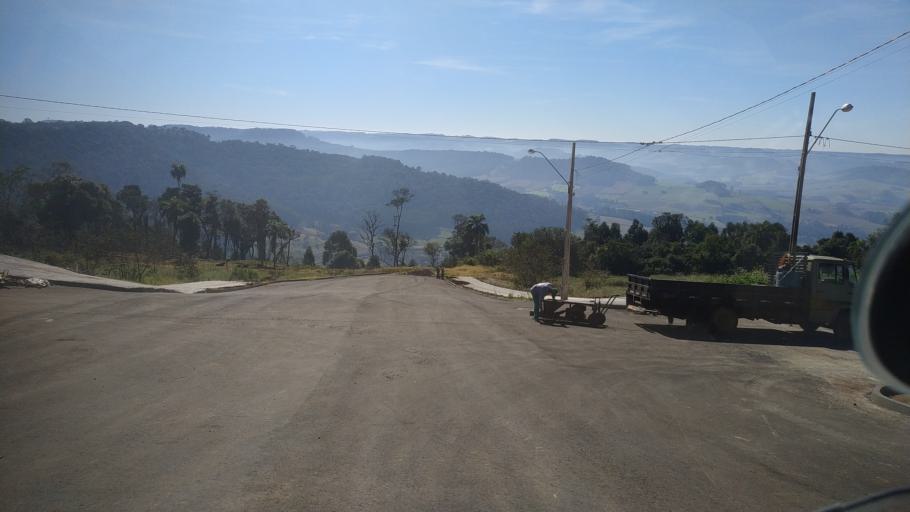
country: BR
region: Santa Catarina
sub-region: Chapeco
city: Chapeco
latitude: -27.0474
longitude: -52.6045
